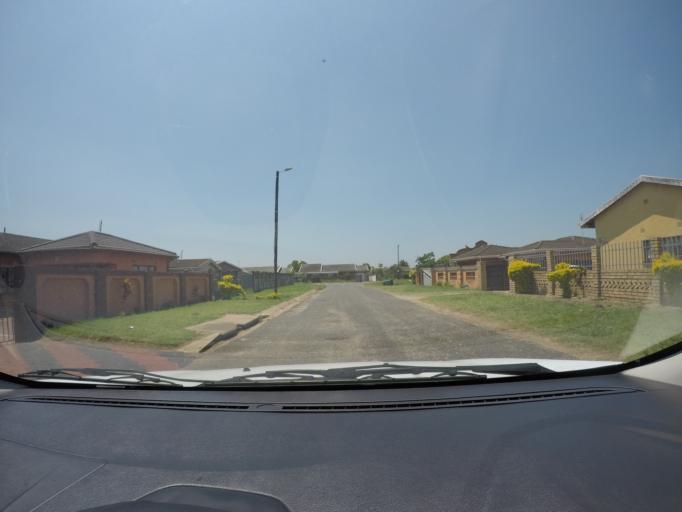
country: ZA
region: KwaZulu-Natal
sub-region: uThungulu District Municipality
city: eSikhawini
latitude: -28.8891
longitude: 31.8844
